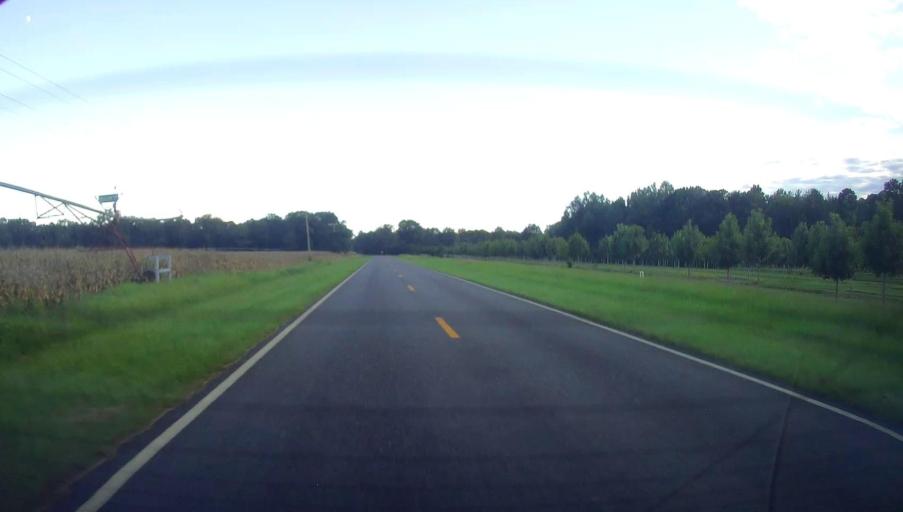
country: US
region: Georgia
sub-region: Pulaski County
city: Hawkinsville
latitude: 32.3007
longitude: -83.5528
